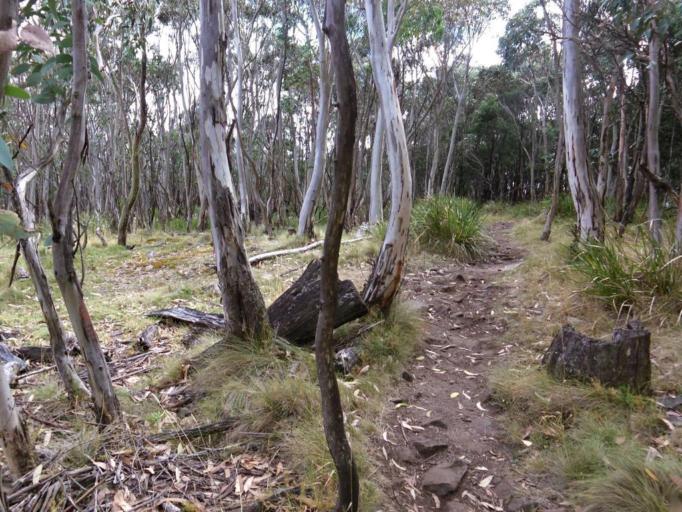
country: AU
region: Victoria
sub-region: Hume
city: Sunbury
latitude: -37.3887
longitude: 144.5765
